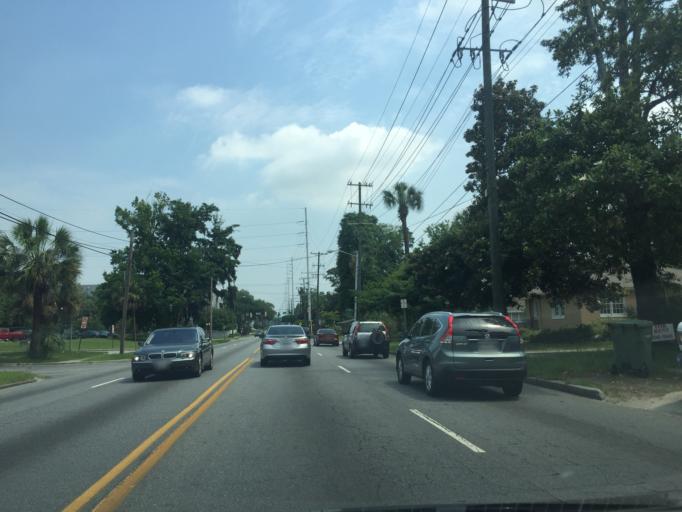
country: US
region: Georgia
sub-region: Chatham County
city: Savannah
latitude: 32.0457
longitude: -81.1091
